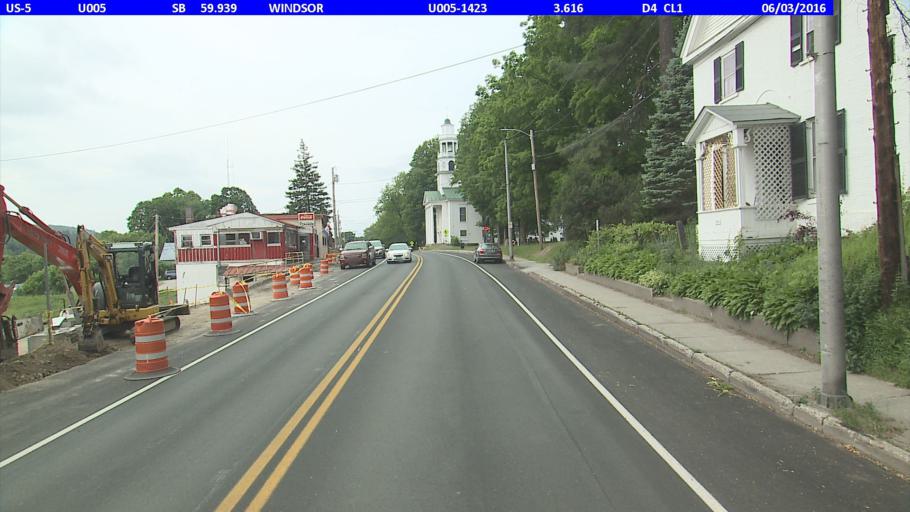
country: US
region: Vermont
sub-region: Windsor County
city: Windsor
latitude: 43.4791
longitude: -72.3870
